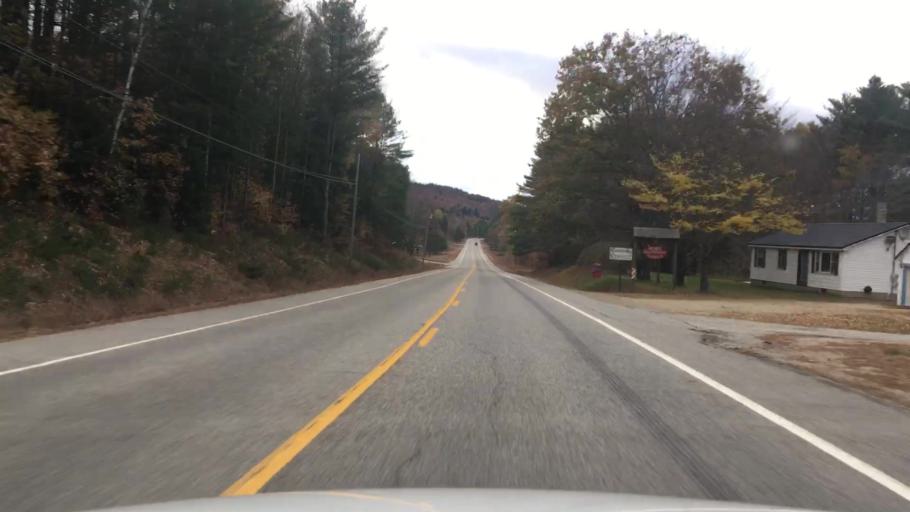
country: US
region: Maine
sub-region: Oxford County
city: Canton
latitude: 44.4159
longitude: -70.2852
